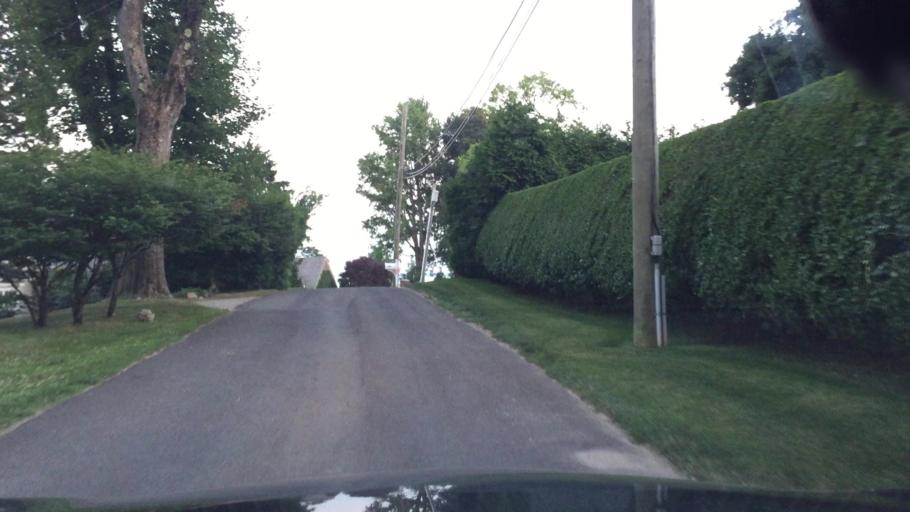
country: US
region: Connecticut
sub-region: Fairfield County
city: Darien
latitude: 41.0666
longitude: -73.4269
